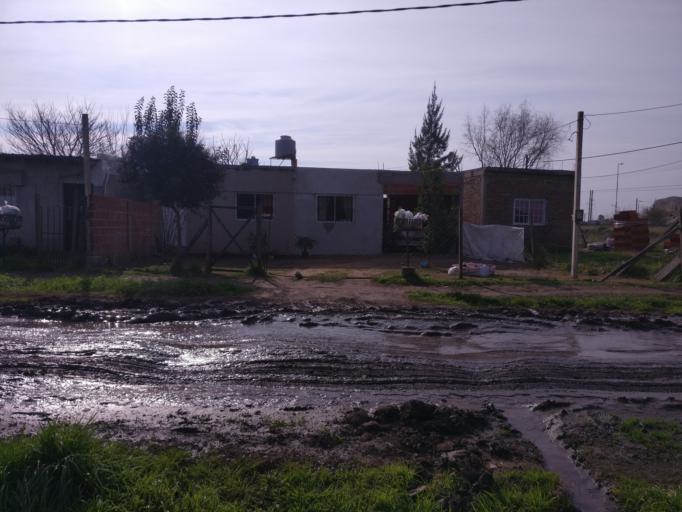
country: AR
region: Buenos Aires
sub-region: Partido de Ezeiza
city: Ezeiza
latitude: -34.9317
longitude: -58.6173
